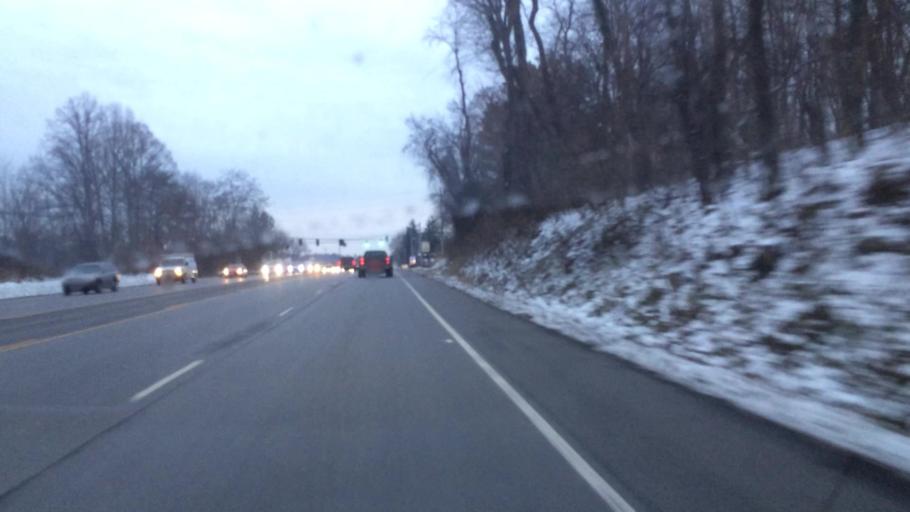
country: US
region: Ohio
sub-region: Summit County
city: Montrose-Ghent
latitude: 41.1359
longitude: -81.6698
